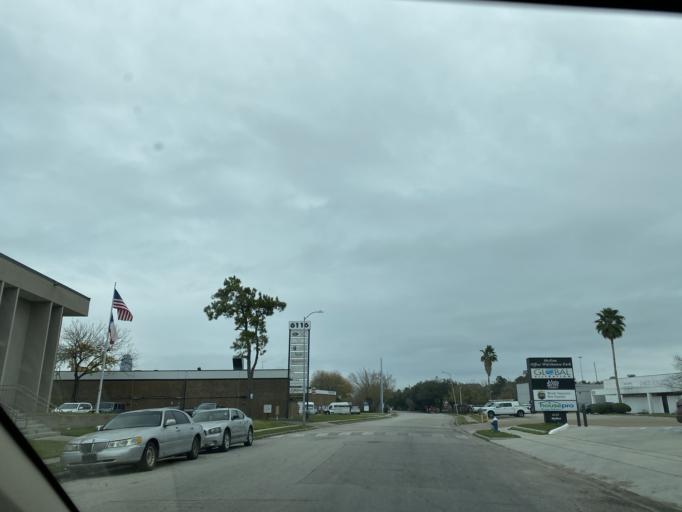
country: US
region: Texas
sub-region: Harris County
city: Bellaire
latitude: 29.7286
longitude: -95.4893
